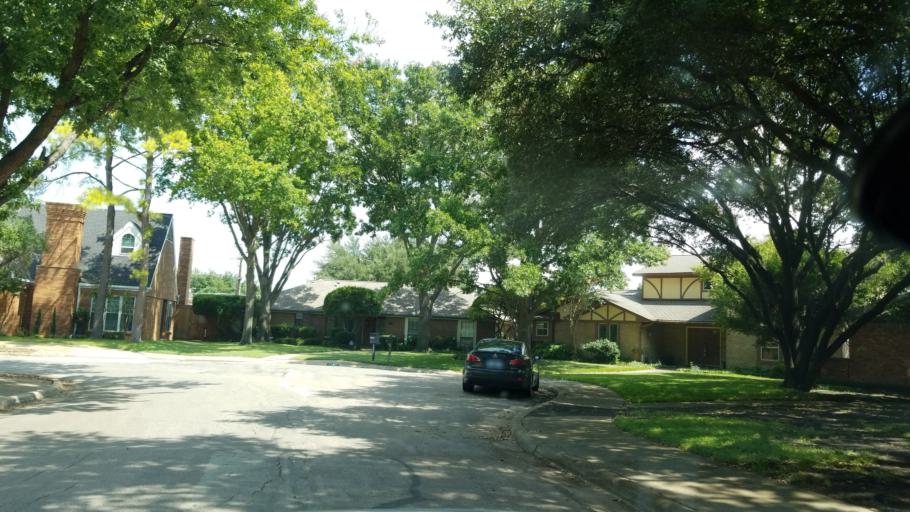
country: US
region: Texas
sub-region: Dallas County
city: Richardson
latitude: 32.9172
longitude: -96.7187
